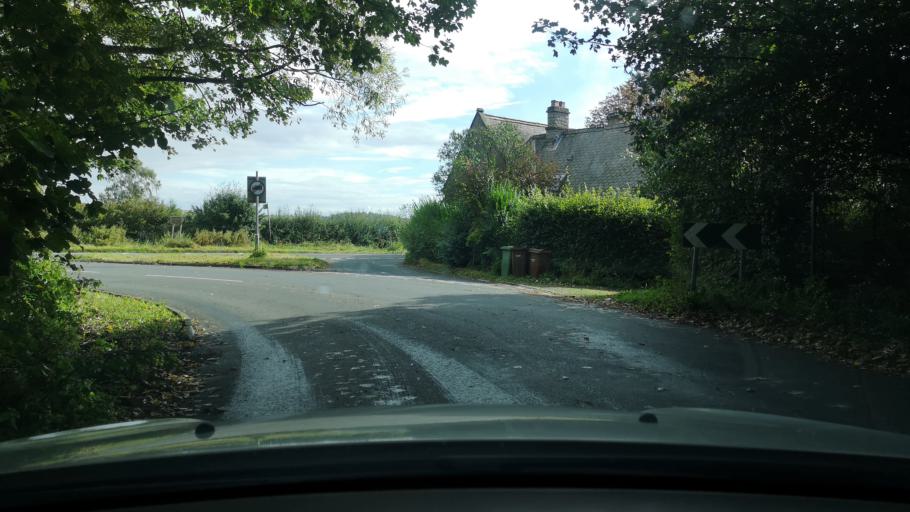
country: GB
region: England
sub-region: City and Borough of Wakefield
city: Low Ackworth
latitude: 53.6584
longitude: -1.3027
